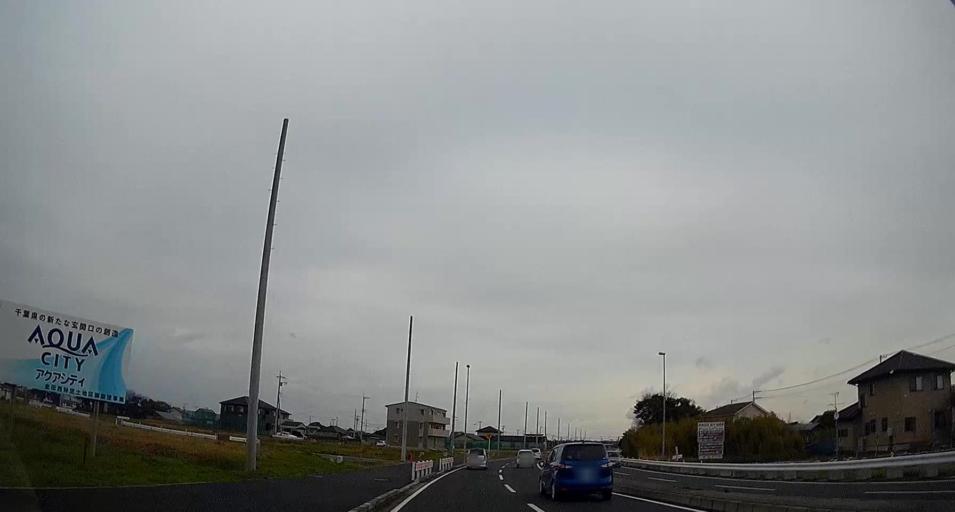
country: JP
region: Chiba
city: Kisarazu
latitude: 35.4241
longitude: 139.9201
